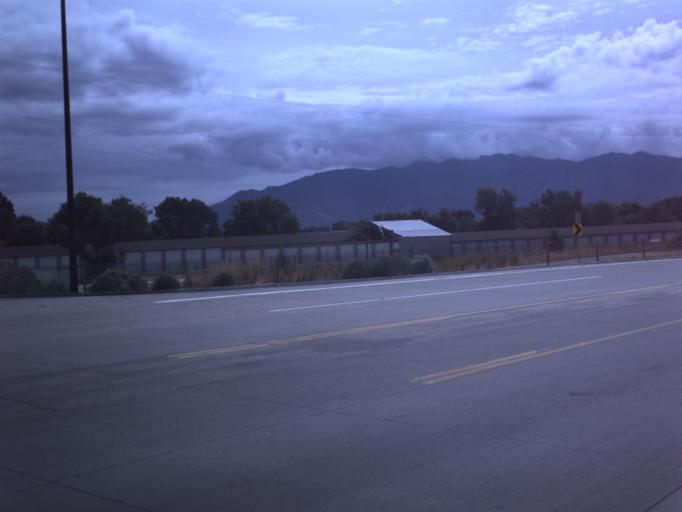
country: US
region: Utah
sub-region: Davis County
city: Clearfield
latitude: 41.1101
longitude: -112.0328
